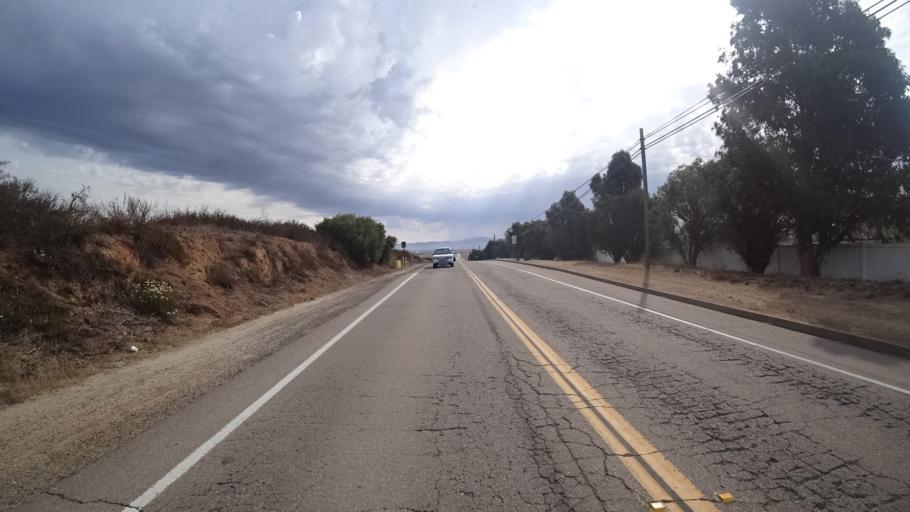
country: US
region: California
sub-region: San Diego County
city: San Pasqual
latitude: 33.0332
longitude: -116.9532
